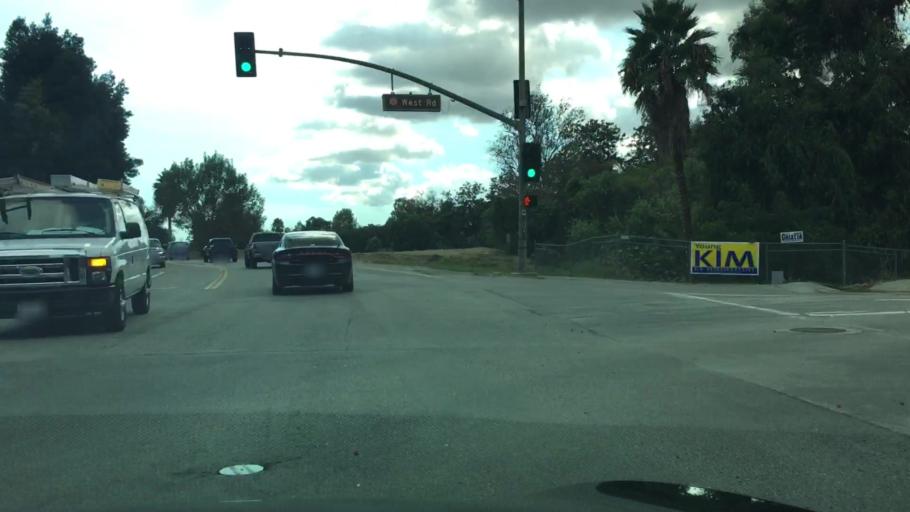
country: US
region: California
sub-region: Los Angeles County
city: La Habra Heights
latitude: 33.9527
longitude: -117.9603
